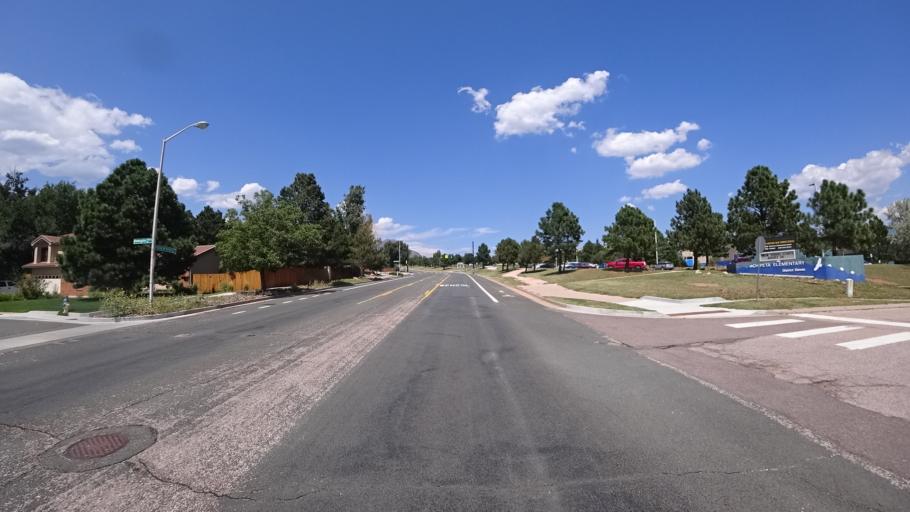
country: US
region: Colorado
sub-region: El Paso County
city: Manitou Springs
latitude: 38.9060
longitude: -104.8720
